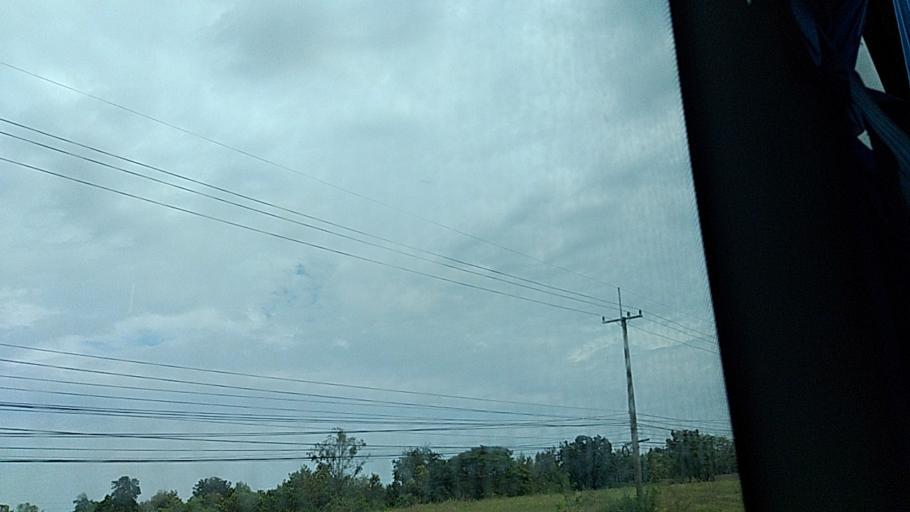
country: TH
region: Kalasin
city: Khong Chai
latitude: 16.1370
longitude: 103.4426
